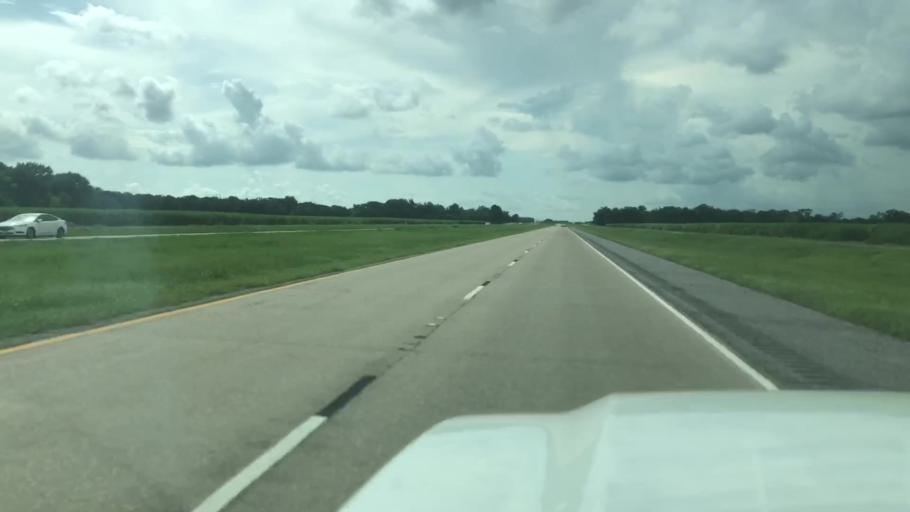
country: US
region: Louisiana
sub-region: Saint Mary Parish
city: Franklin
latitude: 29.7612
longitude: -91.4795
